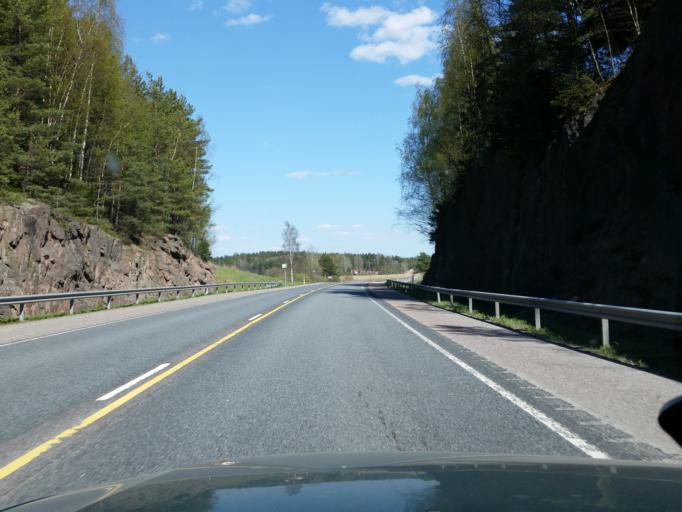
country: FI
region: Uusimaa
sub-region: Helsinki
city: Siuntio
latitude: 60.0793
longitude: 24.1493
